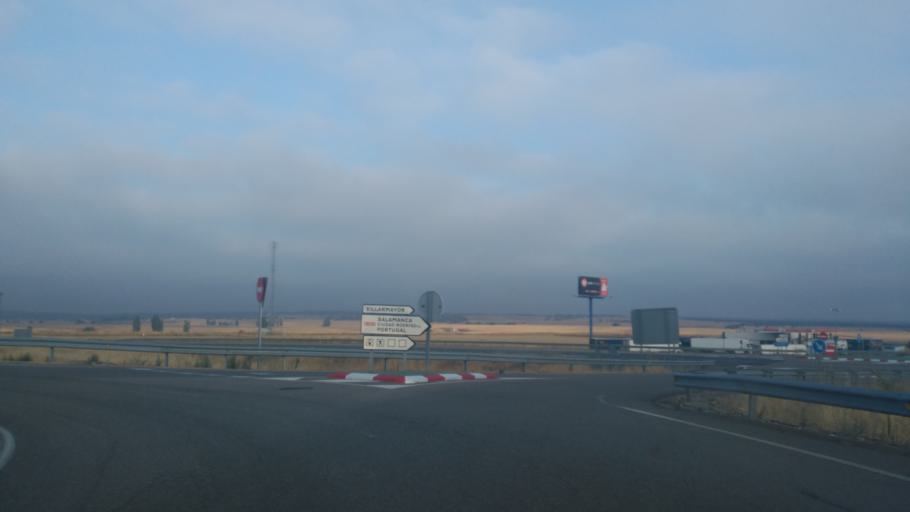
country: ES
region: Castille and Leon
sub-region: Provincia de Salamanca
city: Robliza de Cojos
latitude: 40.8764
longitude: -5.9807
